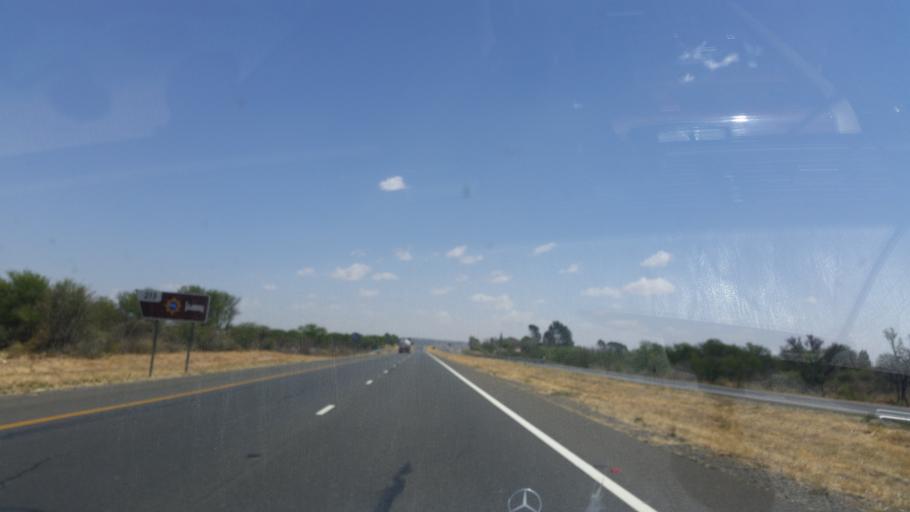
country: ZA
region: Orange Free State
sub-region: Mangaung Metropolitan Municipality
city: Bloemfontein
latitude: -28.9627
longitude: 26.3571
